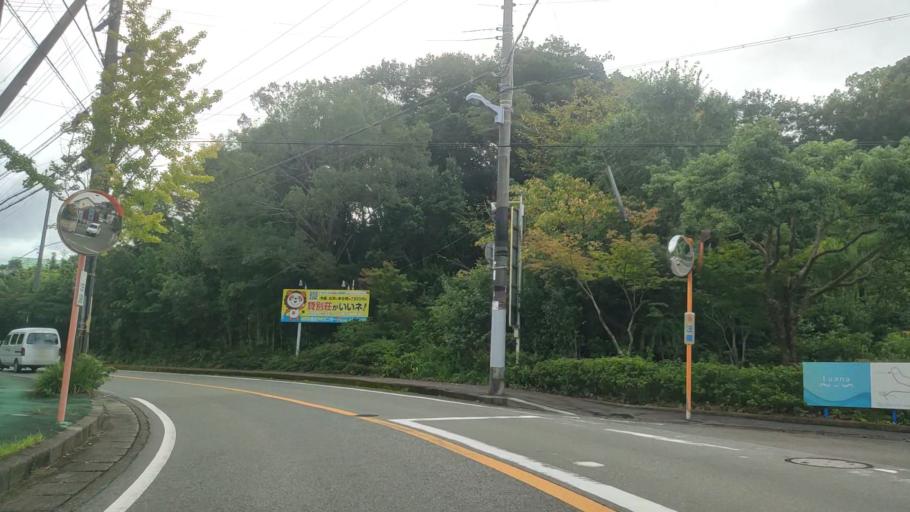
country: JP
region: Wakayama
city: Tanabe
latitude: 33.6770
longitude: 135.3741
